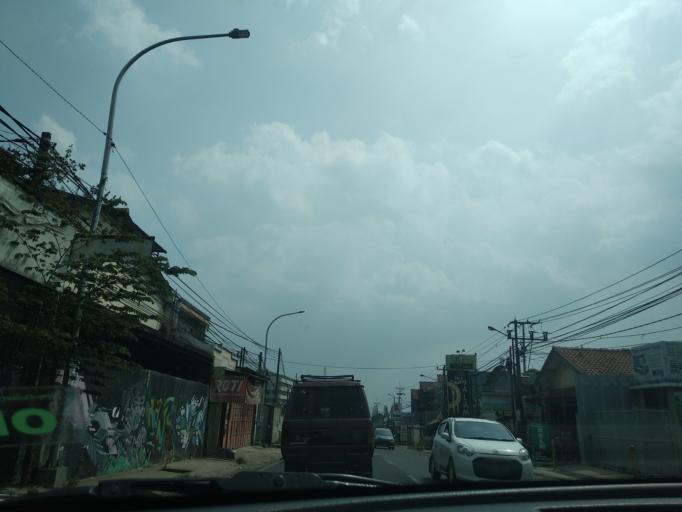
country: ID
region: West Java
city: Cimahi
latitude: -6.8668
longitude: 107.5171
